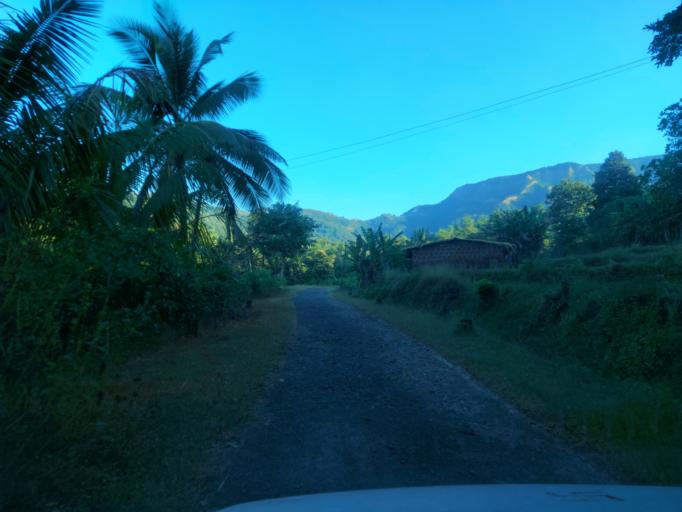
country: IN
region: Maharashtra
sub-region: Sindhudurg
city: Kudal
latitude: 16.0723
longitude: 73.8255
